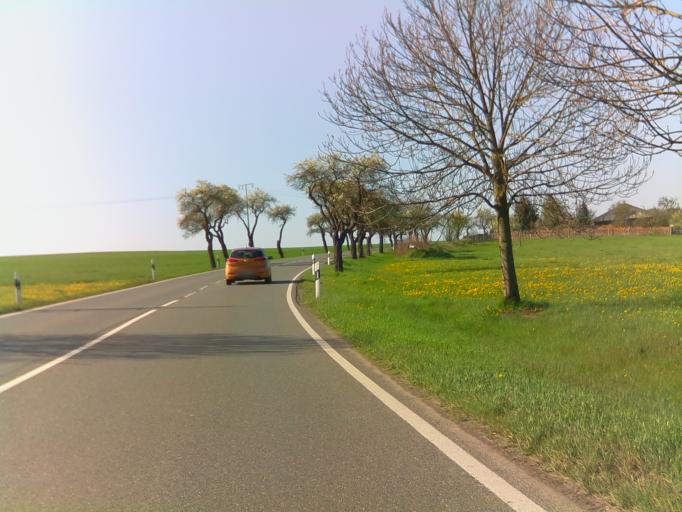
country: DE
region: Thuringia
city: Oettersdorf
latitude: 50.6005
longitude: 11.8248
